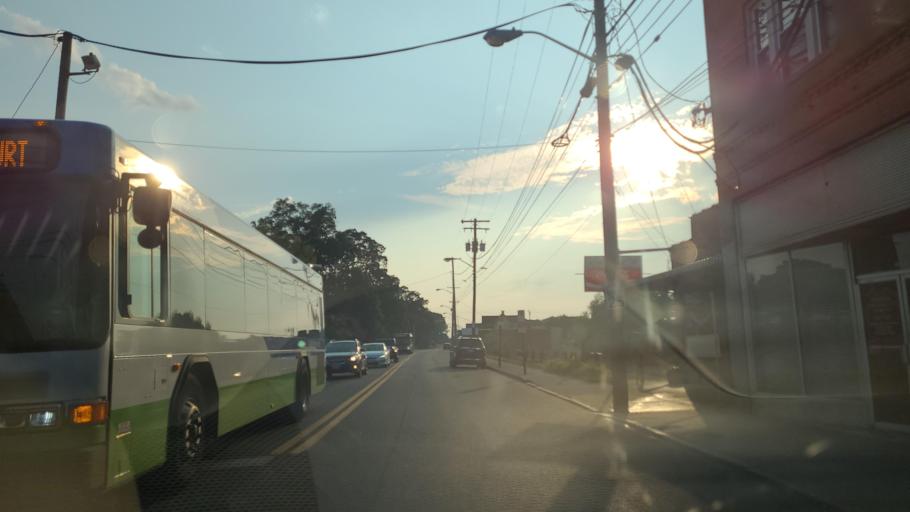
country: US
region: Virginia
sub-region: City of Roanoke
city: Roanoke
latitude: 37.2713
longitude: -79.9501
